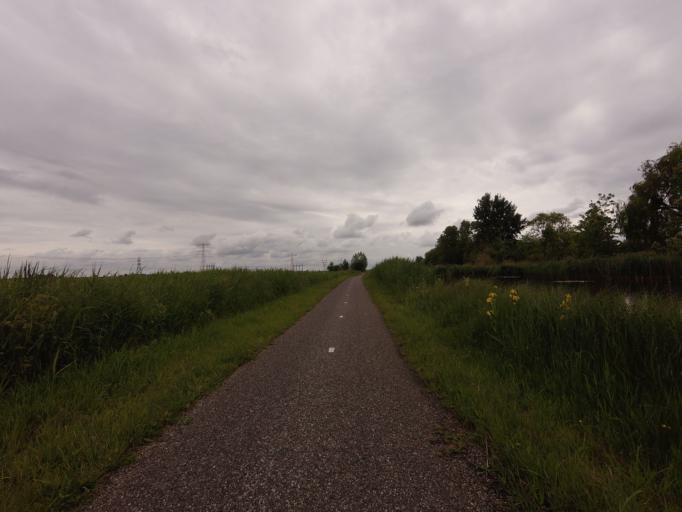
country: NL
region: North Holland
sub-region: Gemeente Waterland
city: Broek in Waterland
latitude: 52.4005
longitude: 4.9627
